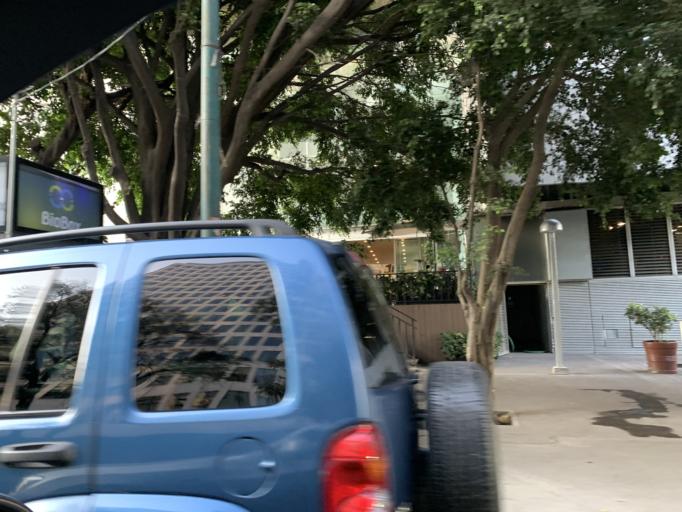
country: MX
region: Mexico City
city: Miguel Hidalgo
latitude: 19.4401
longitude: -99.1845
